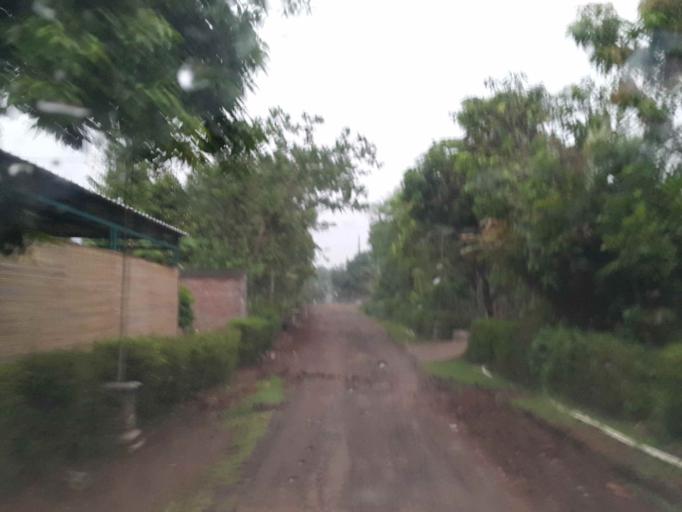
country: ID
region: Central Java
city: Sragen
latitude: -7.5356
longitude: 111.0034
